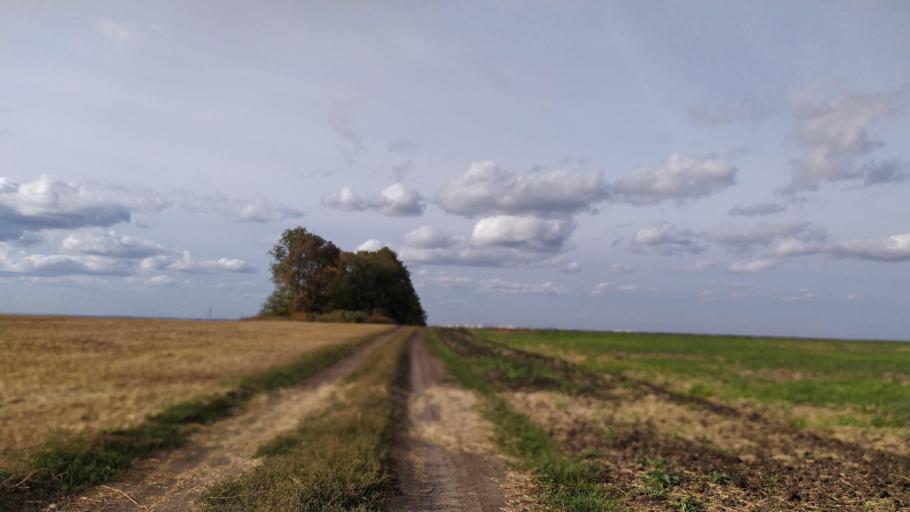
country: RU
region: Kursk
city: Kursk
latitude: 51.6110
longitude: 36.1664
